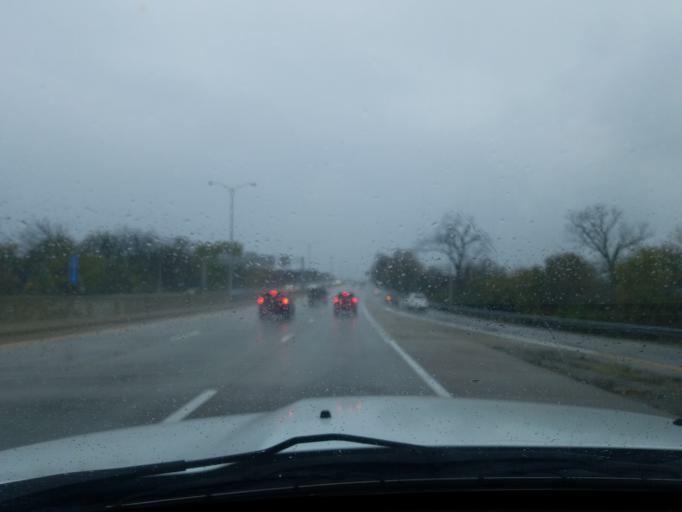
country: US
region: Kentucky
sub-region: Jefferson County
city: Shively
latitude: 38.2366
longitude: -85.8178
